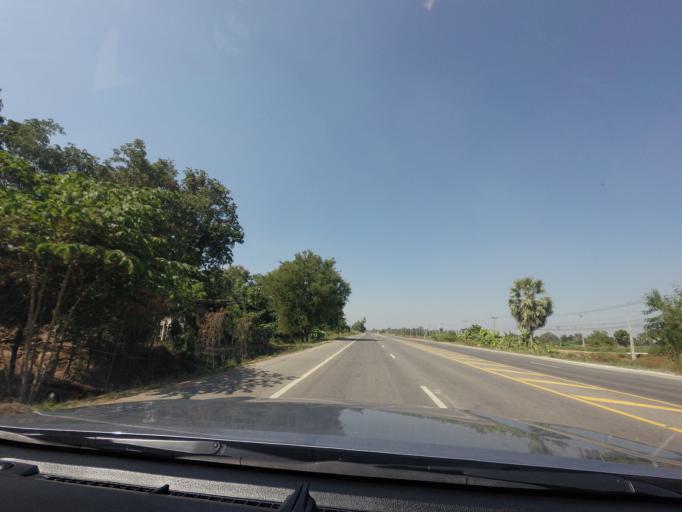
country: TH
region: Sukhothai
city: Ban Na
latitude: 17.0407
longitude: 99.7272
